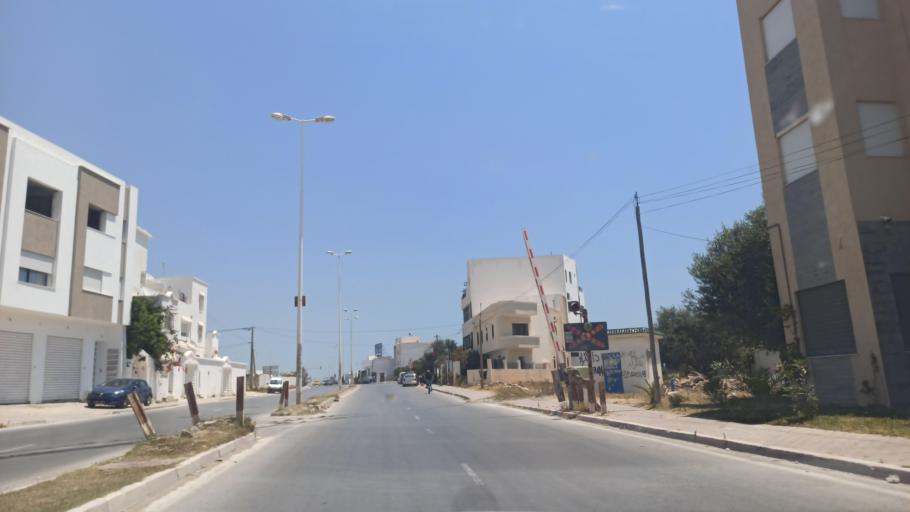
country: TN
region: Nabul
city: Al Hammamat
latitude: 36.4066
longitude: 10.6346
